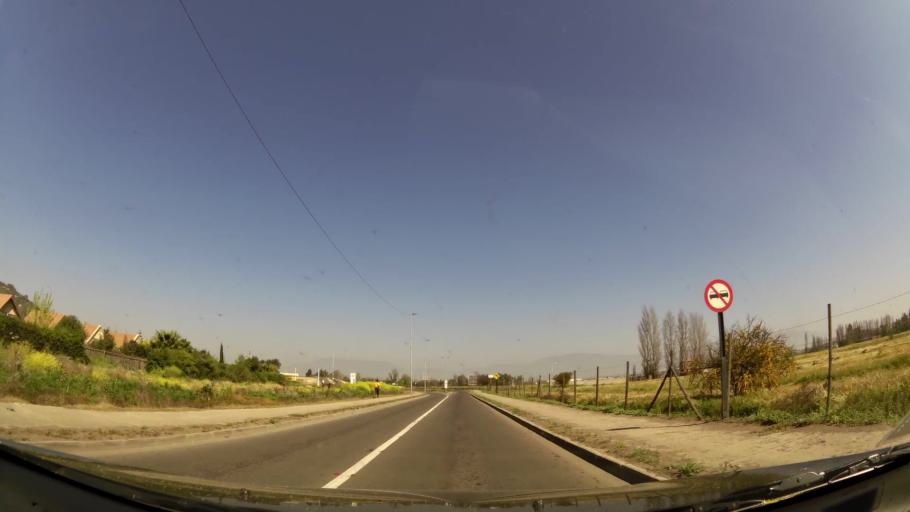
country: CL
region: Santiago Metropolitan
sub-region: Provincia de Chacabuco
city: Chicureo Abajo
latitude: -33.3027
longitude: -70.6950
